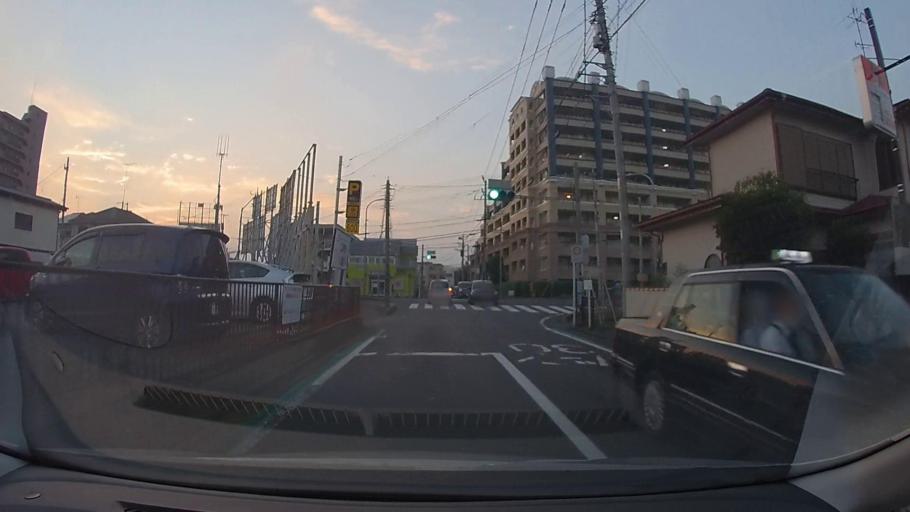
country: JP
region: Kanagawa
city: Minami-rinkan
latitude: 35.5004
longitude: 139.4439
